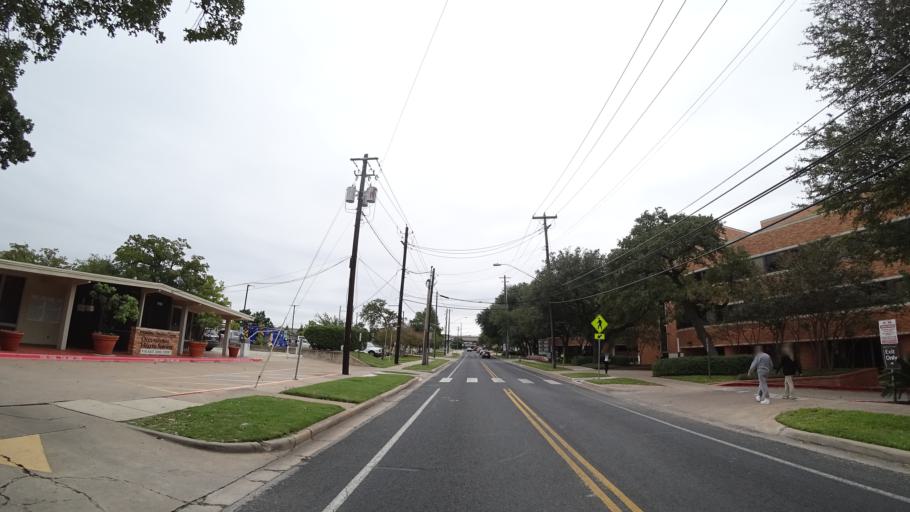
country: US
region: Texas
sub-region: Travis County
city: Austin
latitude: 30.2904
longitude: -97.7256
